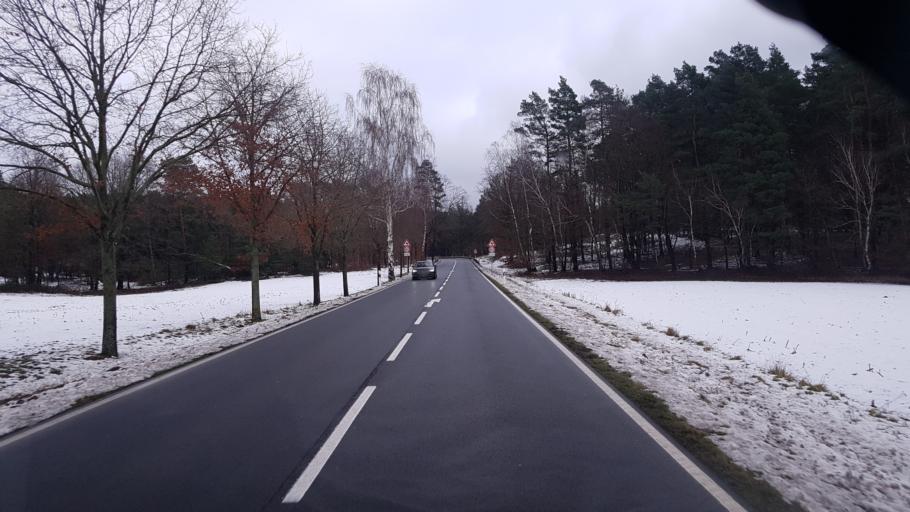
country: DE
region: Brandenburg
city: Schenkendobern
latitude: 51.9766
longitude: 14.5461
